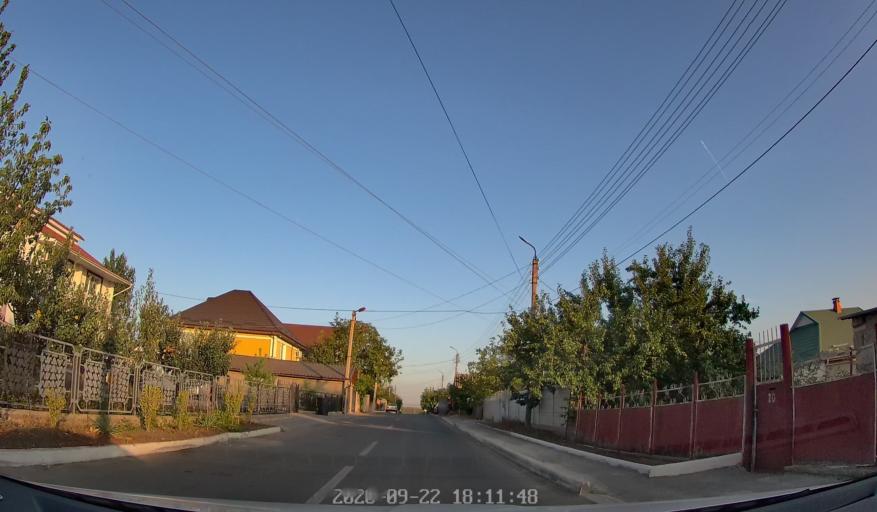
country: MD
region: Laloveni
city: Ialoveni
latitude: 46.9490
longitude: 28.7846
